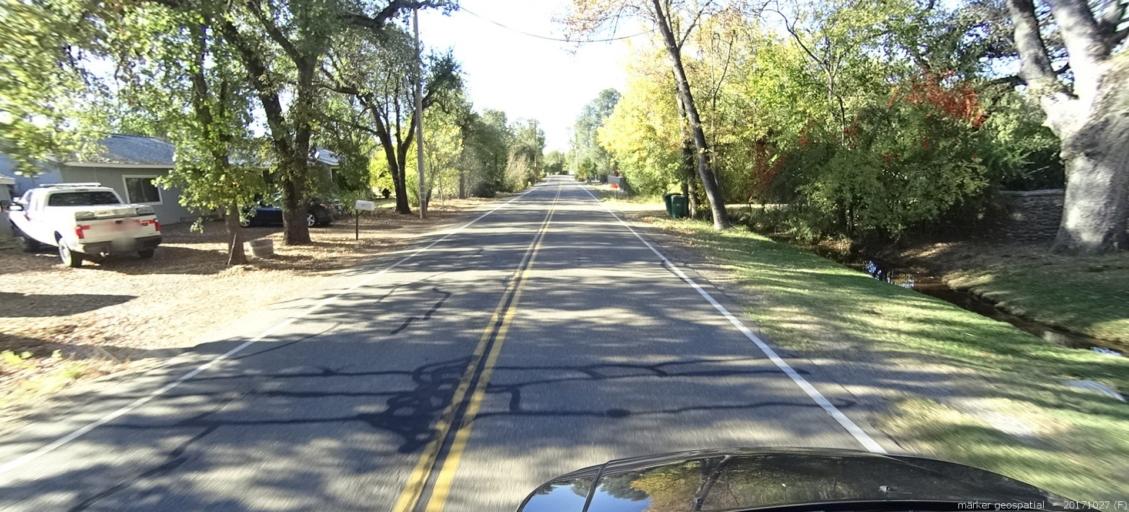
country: US
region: California
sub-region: Shasta County
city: Palo Cedro
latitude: 40.5514
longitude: -122.1821
